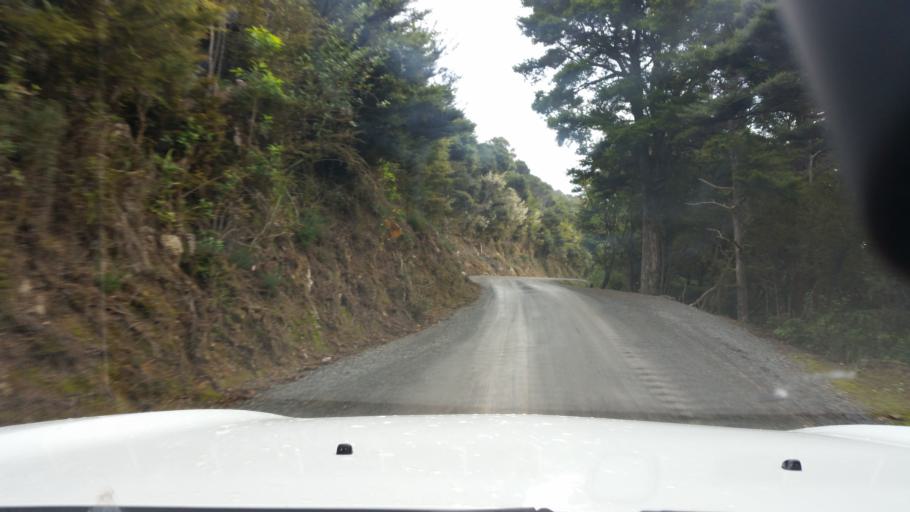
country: NZ
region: Northland
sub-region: Whangarei
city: Ruakaka
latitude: -35.7739
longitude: 174.5367
